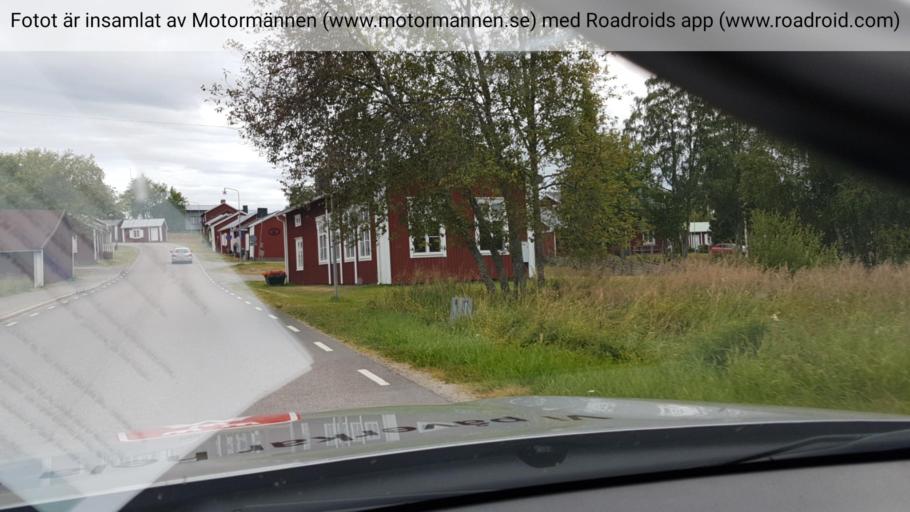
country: SE
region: Norrbotten
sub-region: Lulea Kommun
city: Gammelstad
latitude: 65.6479
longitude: 22.0280
